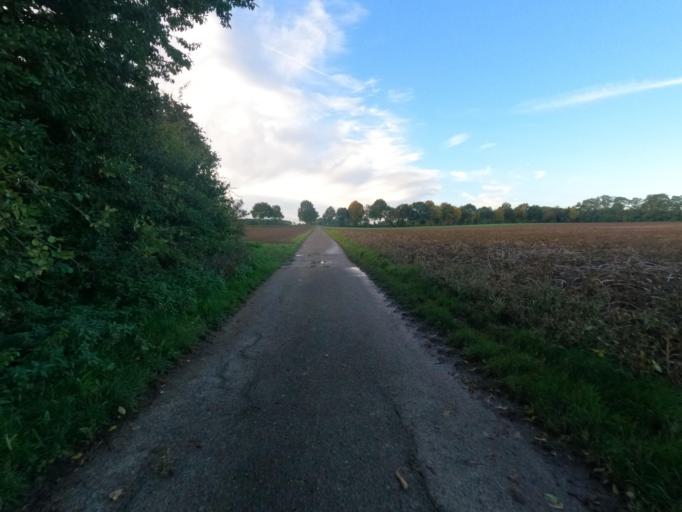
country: DE
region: North Rhine-Westphalia
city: Erkelenz
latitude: 51.0612
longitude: 6.3231
